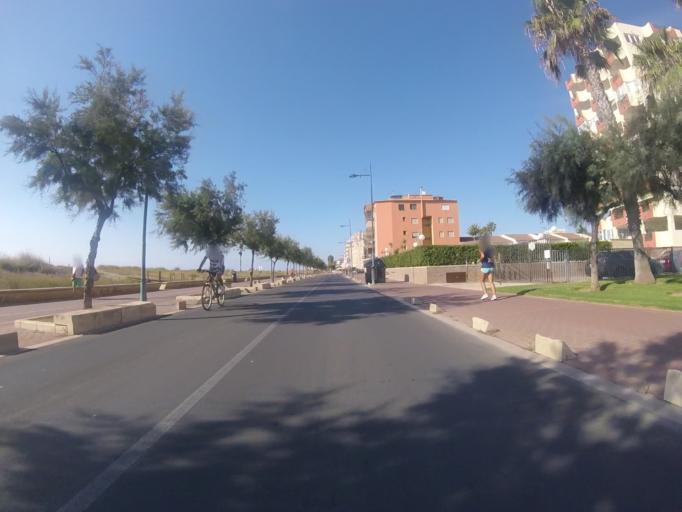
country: ES
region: Valencia
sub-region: Provincia de Castello
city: Benicarlo
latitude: 40.3897
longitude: 0.4119
